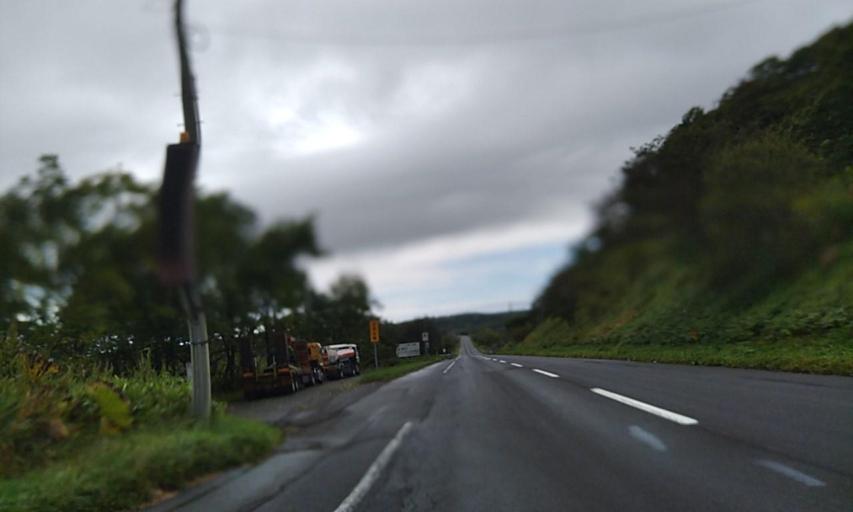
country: JP
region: Hokkaido
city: Kushiro
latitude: 42.8768
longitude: 143.9131
